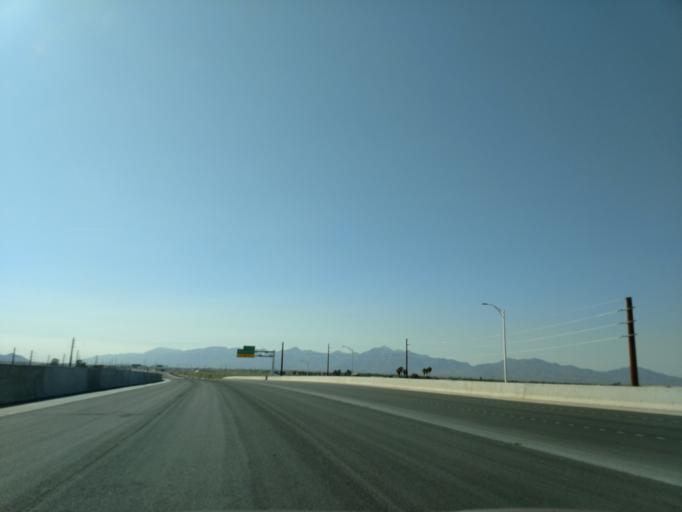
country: US
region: Arizona
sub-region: Maricopa County
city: Tolleson
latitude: 33.4439
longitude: -112.1871
